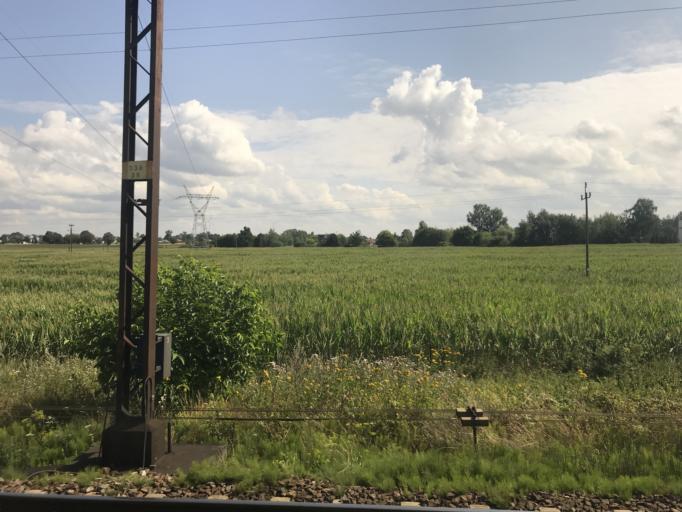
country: PL
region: Kujawsko-Pomorskie
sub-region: Powiat inowroclawski
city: Zlotniki Kujawskie
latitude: 52.9113
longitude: 18.1389
